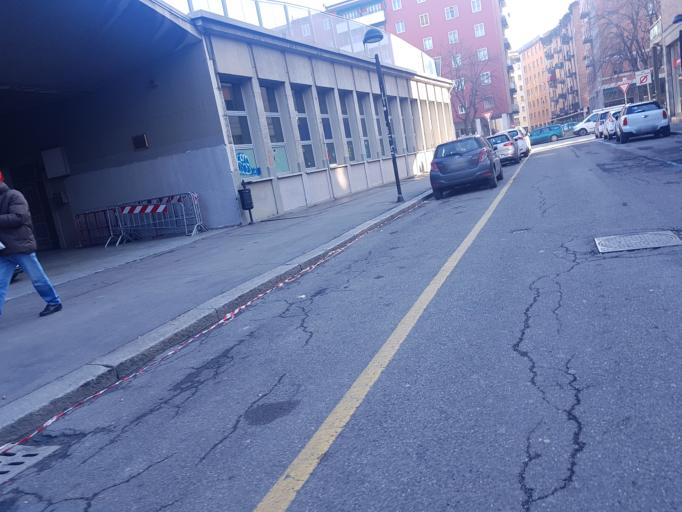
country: IT
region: Emilia-Romagna
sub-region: Provincia di Bologna
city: Bologna
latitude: 44.4994
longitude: 11.3321
